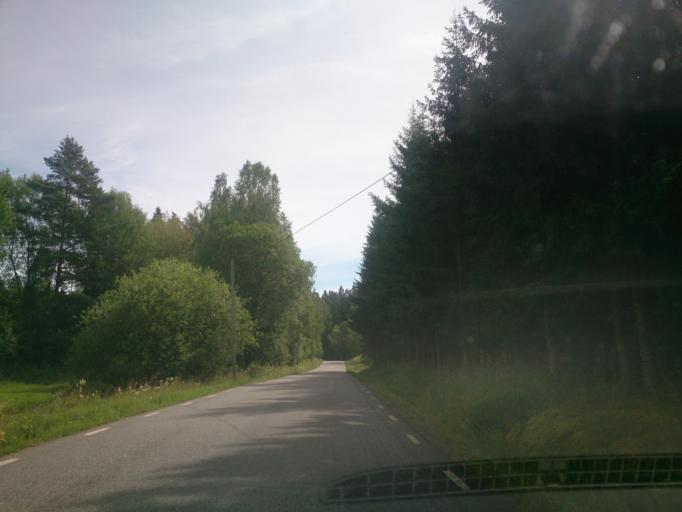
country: SE
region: OEstergoetland
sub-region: Soderkopings Kommun
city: Soederkoeping
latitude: 58.3160
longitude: 16.3192
